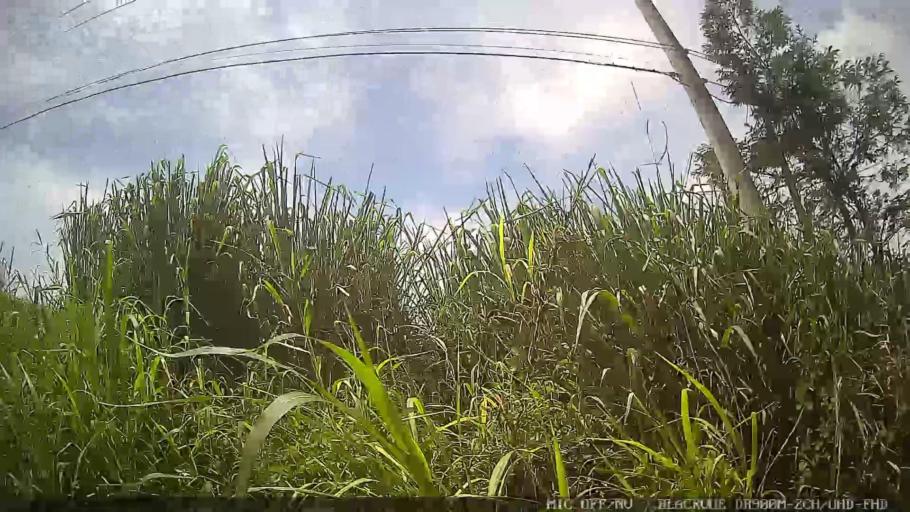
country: BR
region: Sao Paulo
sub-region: Santa Isabel
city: Santa Isabel
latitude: -23.3513
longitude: -46.1795
